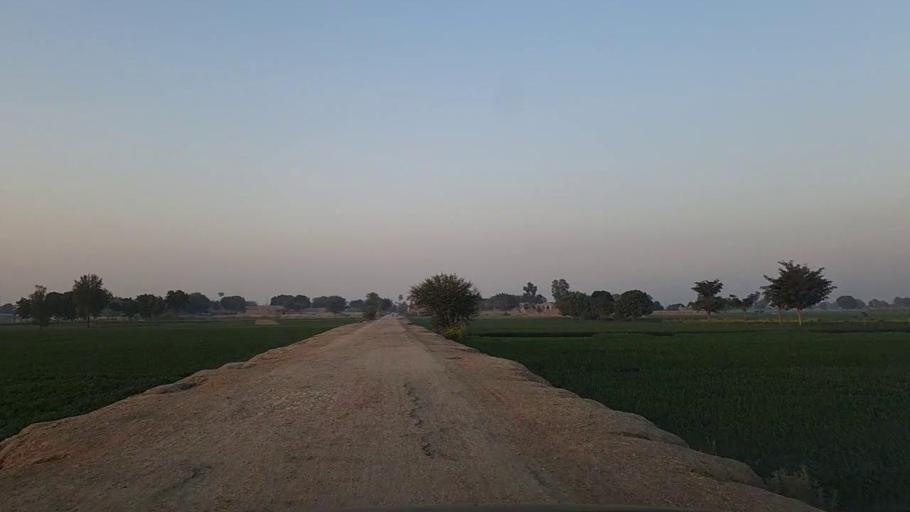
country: PK
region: Sindh
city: Jam Sahib
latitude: 26.4673
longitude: 68.5420
